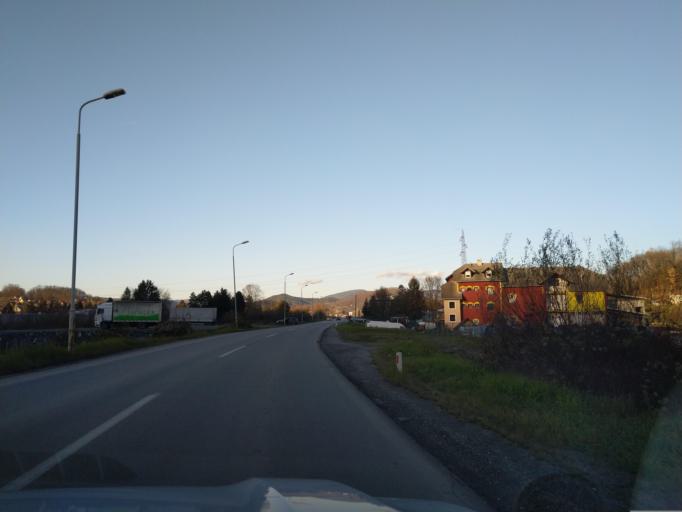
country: RS
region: Central Serbia
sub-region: Zlatiborski Okrug
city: Kosjeric
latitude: 43.9963
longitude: 19.9160
